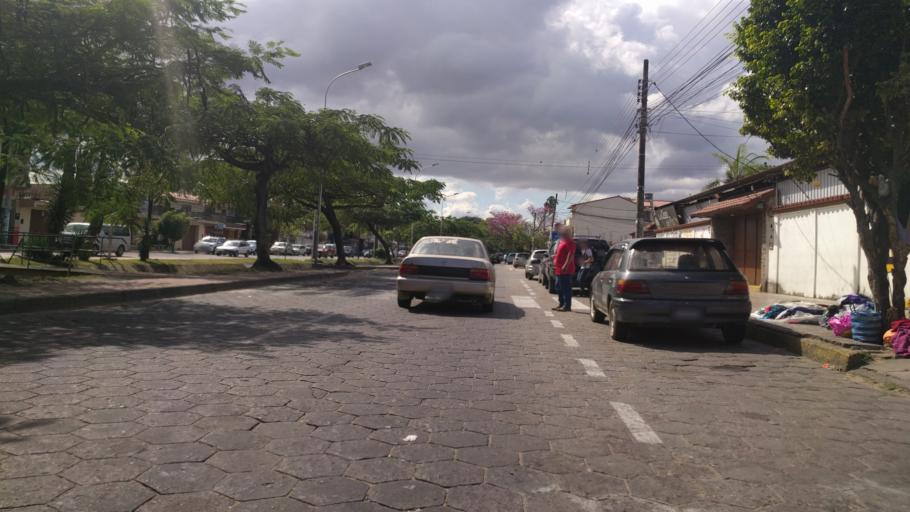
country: BO
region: Santa Cruz
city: Santa Cruz de la Sierra
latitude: -17.7940
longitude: -63.2033
